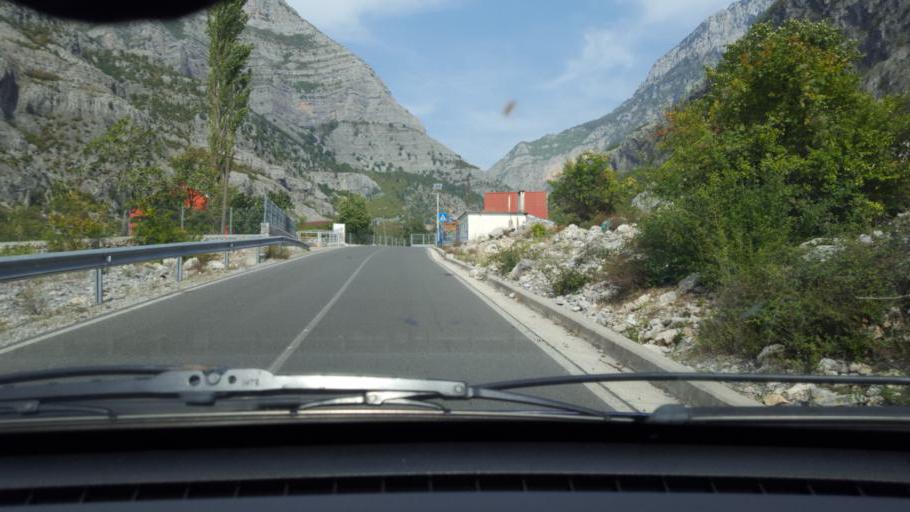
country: AL
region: Shkoder
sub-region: Rrethi i Malesia e Madhe
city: Kastrat
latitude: 42.4657
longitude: 19.5645
